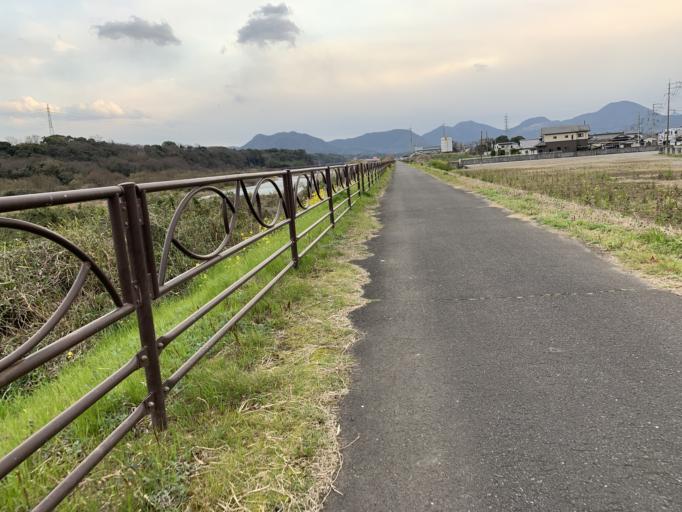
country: JP
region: Oita
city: Bungo-Takada-shi
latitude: 33.5406
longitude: 131.3538
